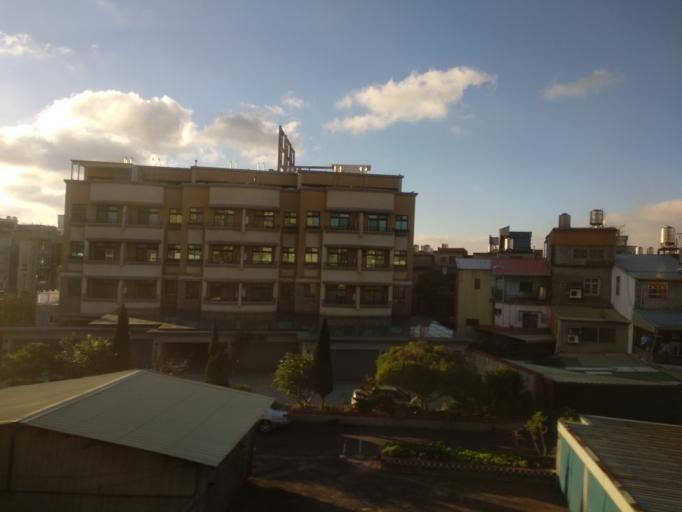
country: TW
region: Taiwan
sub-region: Hsinchu
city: Zhubei
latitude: 24.8284
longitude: 121.0015
